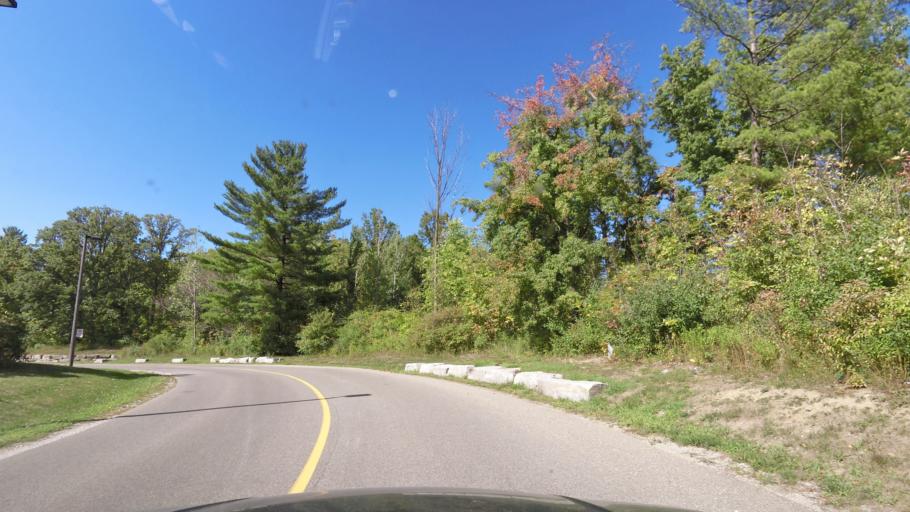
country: CA
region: Ontario
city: Mississauga
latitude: 43.5656
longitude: -79.6696
